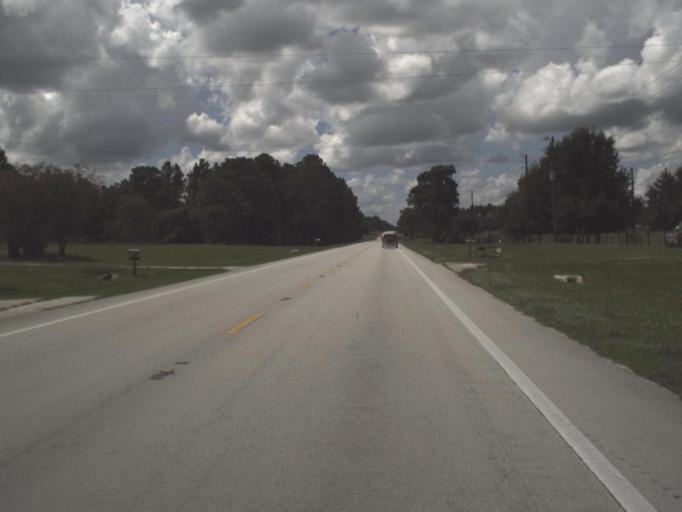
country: US
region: Florida
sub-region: Polk County
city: Polk City
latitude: 28.3219
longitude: -81.8343
